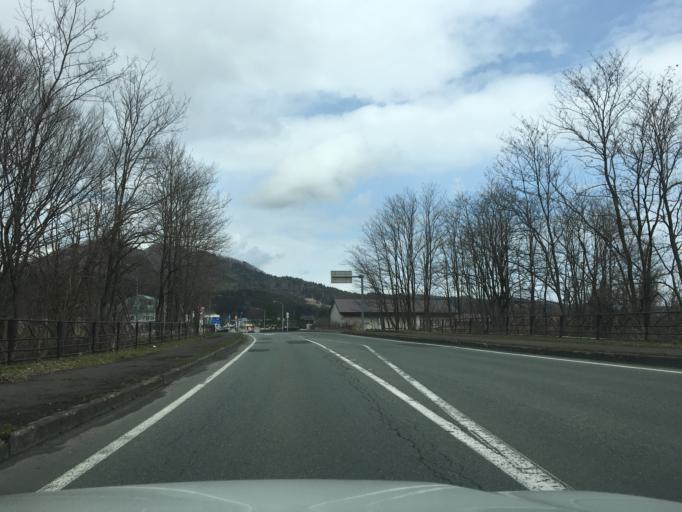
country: JP
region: Akita
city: Tenno
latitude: 39.9396
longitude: 140.1118
